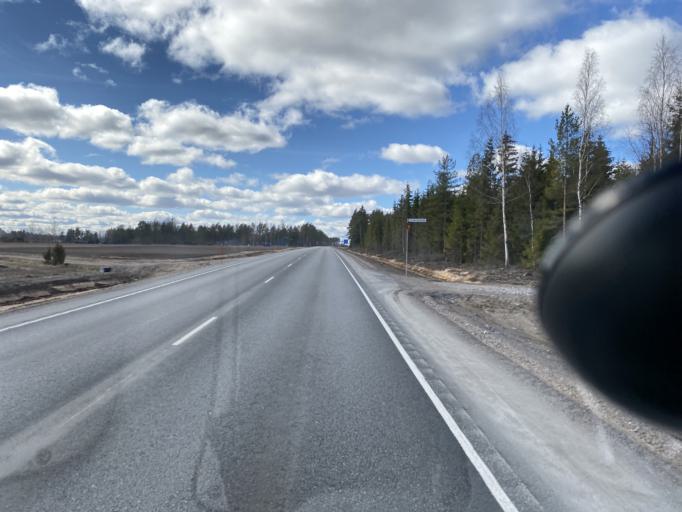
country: FI
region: Satakunta
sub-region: Rauma
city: Koeylioe
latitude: 61.1605
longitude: 22.2998
